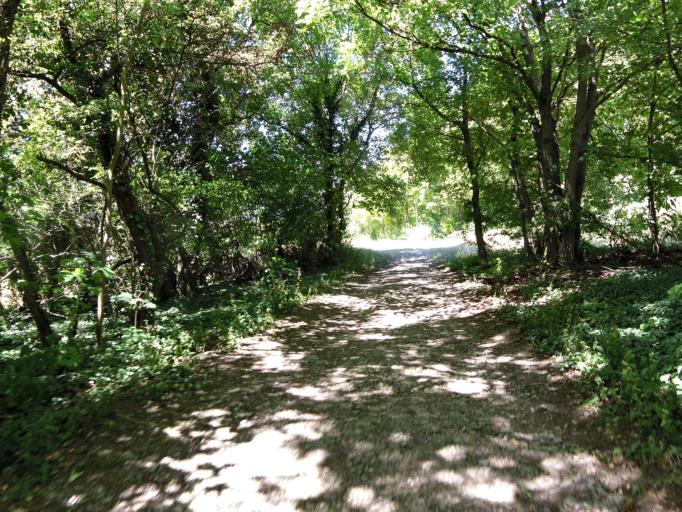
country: DE
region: Bavaria
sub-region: Regierungsbezirk Unterfranken
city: Hochberg
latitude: 49.7791
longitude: 9.9151
